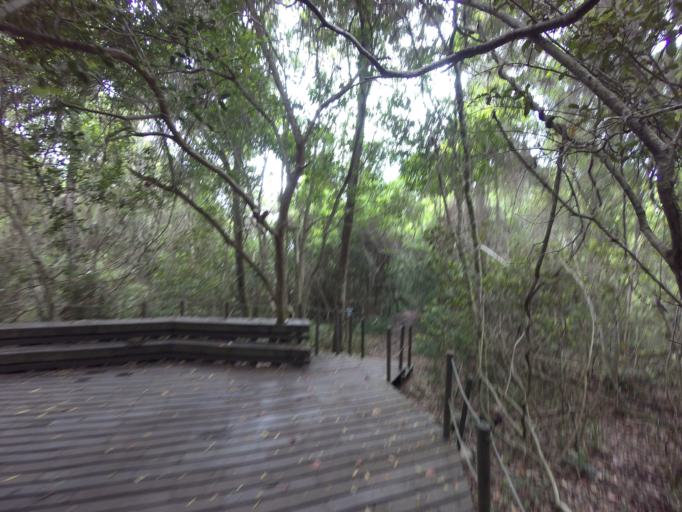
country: ZA
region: Eastern Cape
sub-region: Cacadu District Municipality
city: Kareedouw
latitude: -34.0211
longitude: 23.8983
